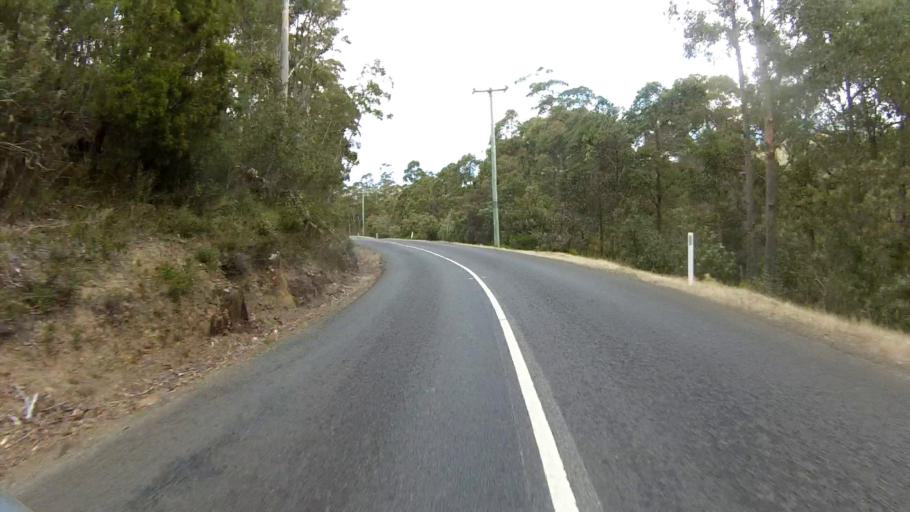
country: AU
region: Tasmania
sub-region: Kingborough
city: Margate
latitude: -42.9753
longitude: 147.1773
